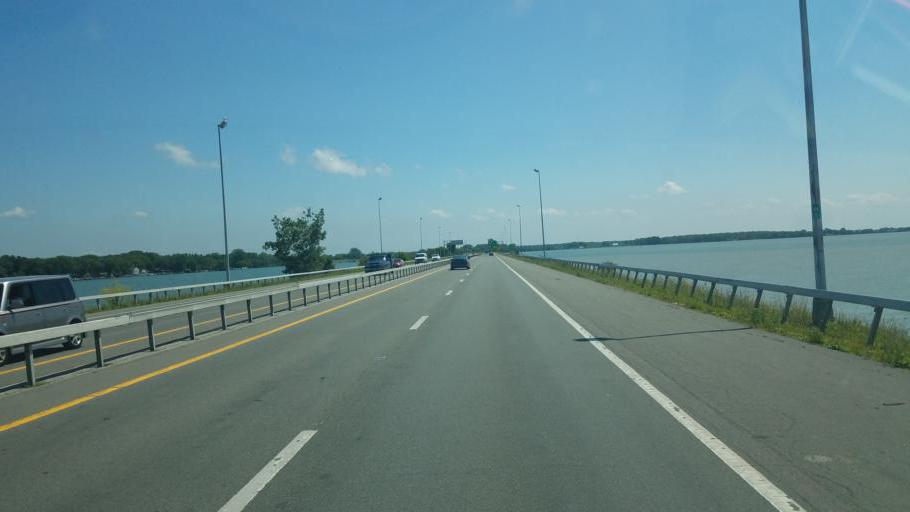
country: US
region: Ohio
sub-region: Ottawa County
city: Port Clinton
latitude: 41.4735
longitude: -82.8337
